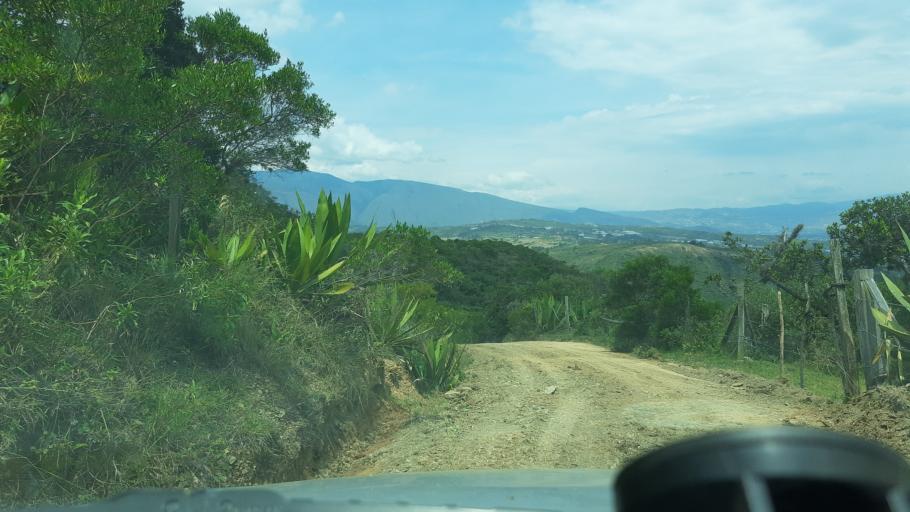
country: CO
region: Boyaca
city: Santa Sofia
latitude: 5.6964
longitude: -73.5807
